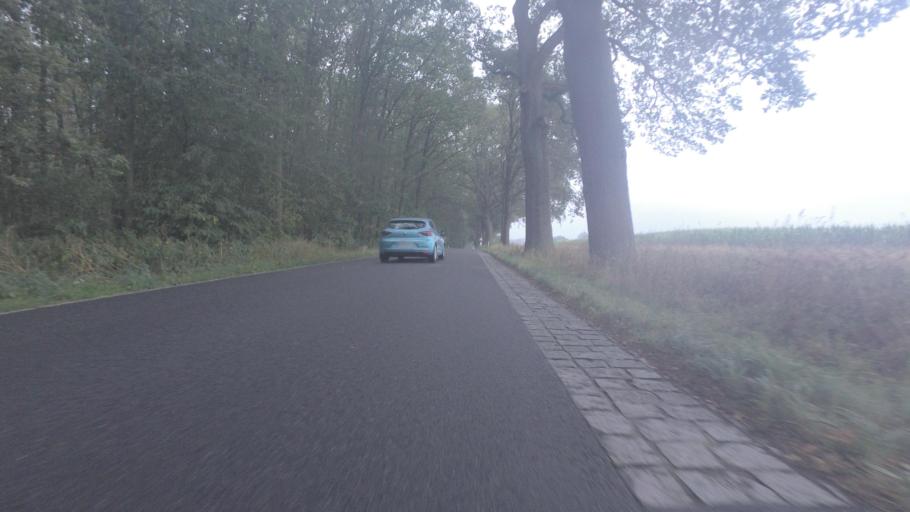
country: DE
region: Brandenburg
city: Heiligengrabe
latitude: 53.1534
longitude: 12.3442
